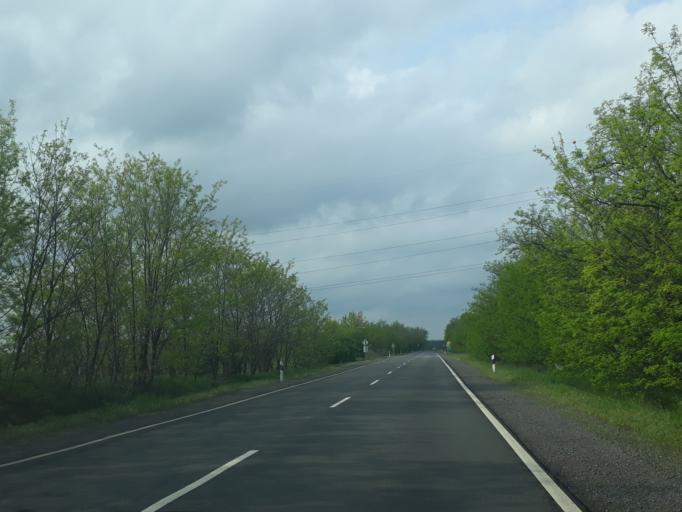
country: HU
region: Szabolcs-Szatmar-Bereg
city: Patroha
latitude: 48.1555
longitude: 22.0281
